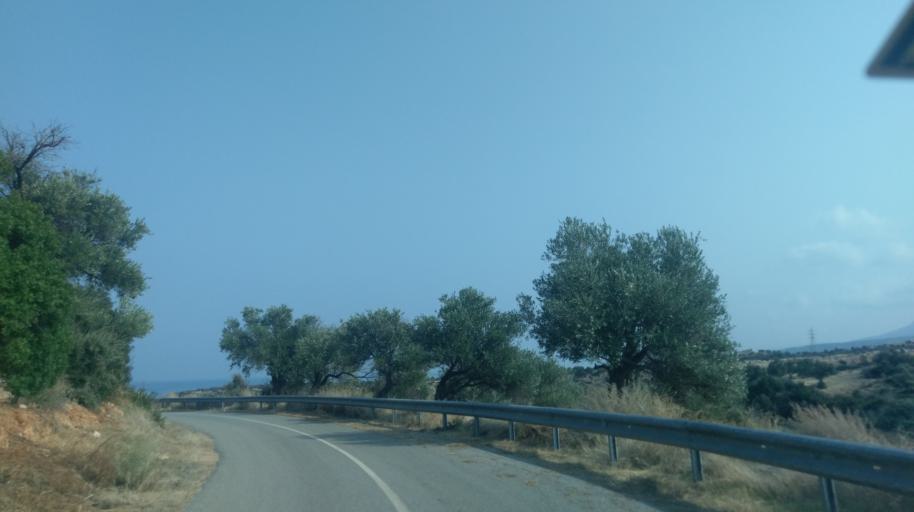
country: CY
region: Keryneia
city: Kyrenia
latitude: 35.3209
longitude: 33.4687
